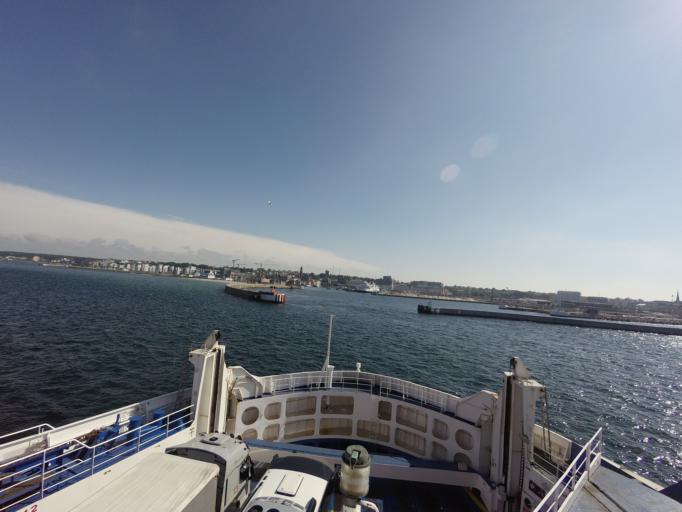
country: SE
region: Skane
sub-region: Helsingborg
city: Helsingborg
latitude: 56.0398
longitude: 12.6831
